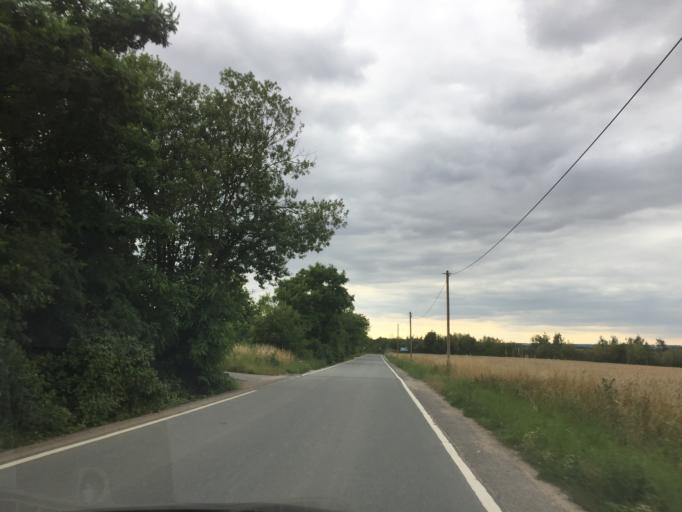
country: DE
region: Thuringia
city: Schmolln
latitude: 50.8754
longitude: 12.3439
